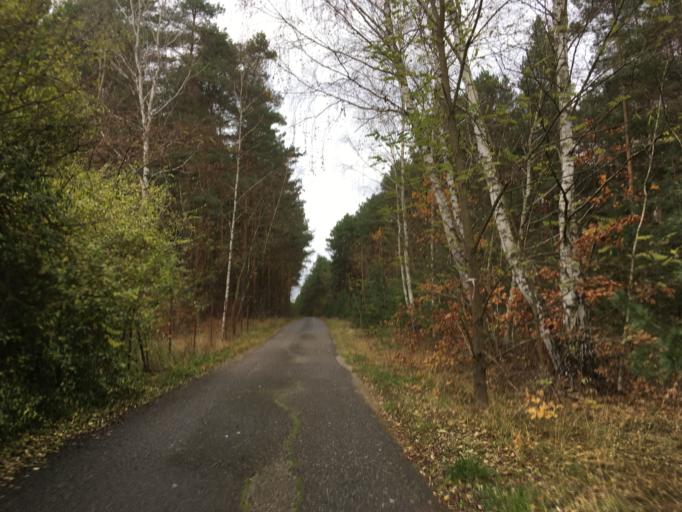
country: DE
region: Brandenburg
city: Mixdorf
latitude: 52.1021
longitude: 14.4320
